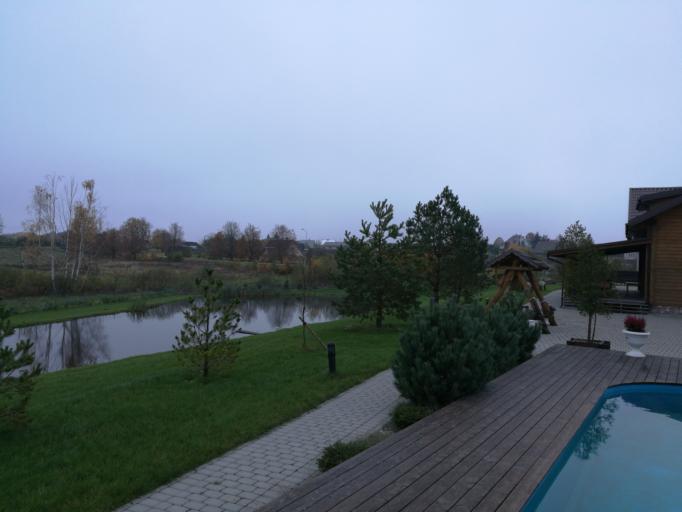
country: LT
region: Vilnius County
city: Elektrenai
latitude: 54.7789
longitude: 24.7199
